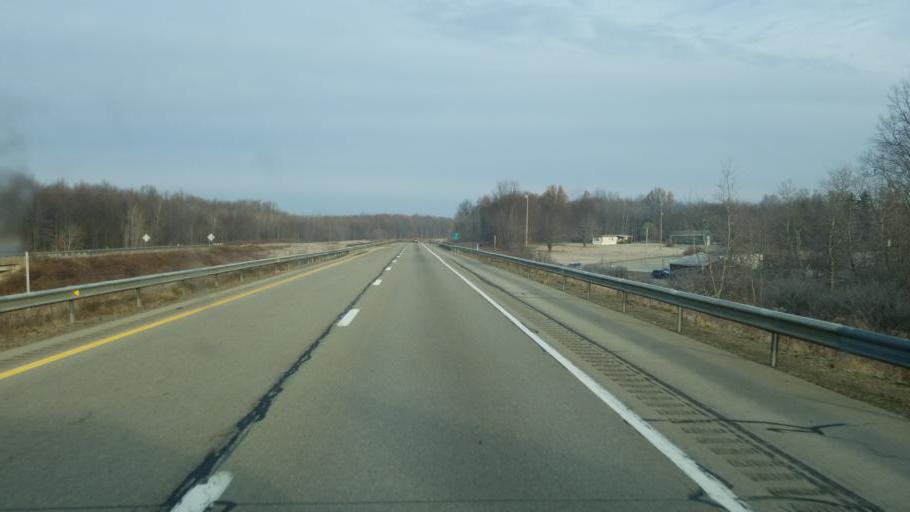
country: US
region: Pennsylvania
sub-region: Crawford County
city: Cochranton
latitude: 41.5052
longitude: -80.1701
